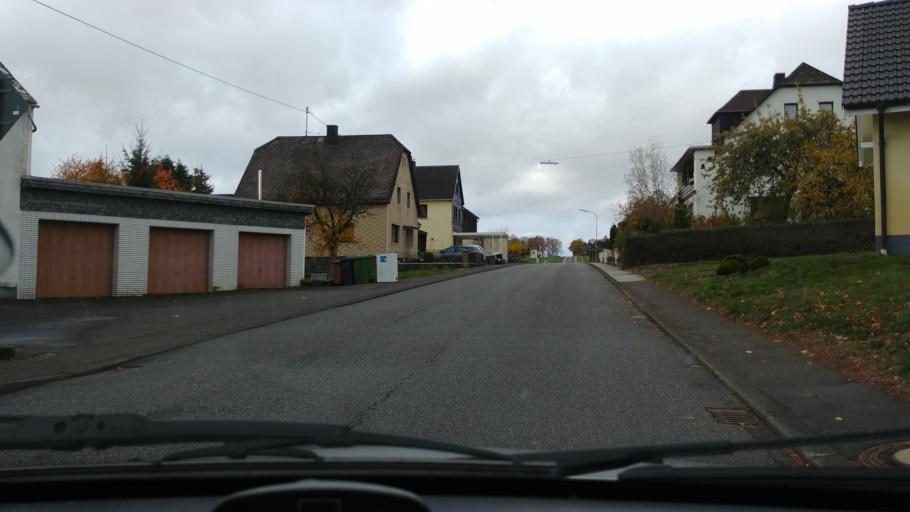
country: DE
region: Rheinland-Pfalz
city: Stockhausen-Illfurth
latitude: 50.6464
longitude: 7.9882
